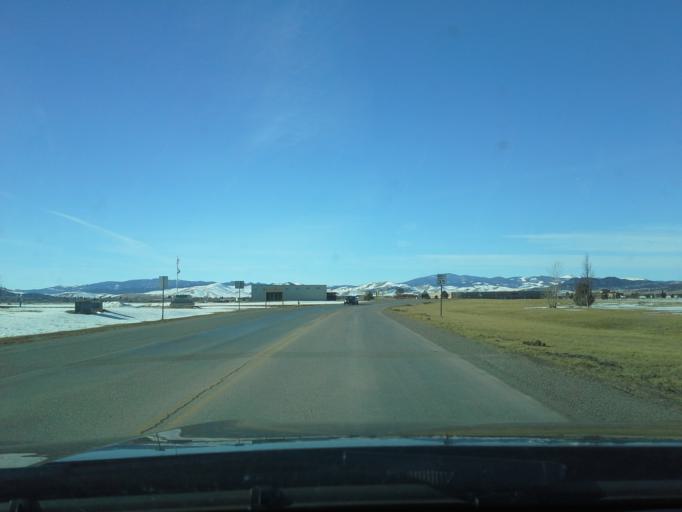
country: US
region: Montana
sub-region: Lewis and Clark County
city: Helena
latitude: 46.6120
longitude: -111.9918
